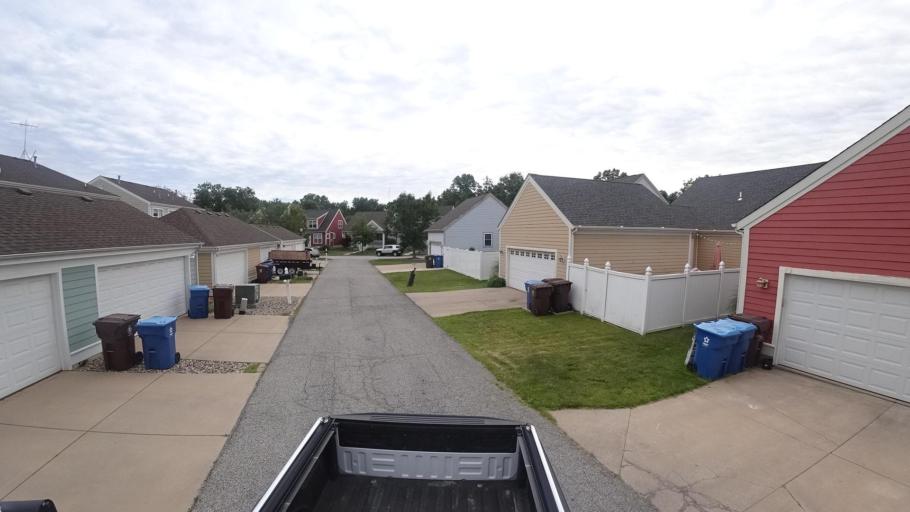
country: US
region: Indiana
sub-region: Porter County
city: Burns Harbor
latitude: 41.6023
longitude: -87.1309
